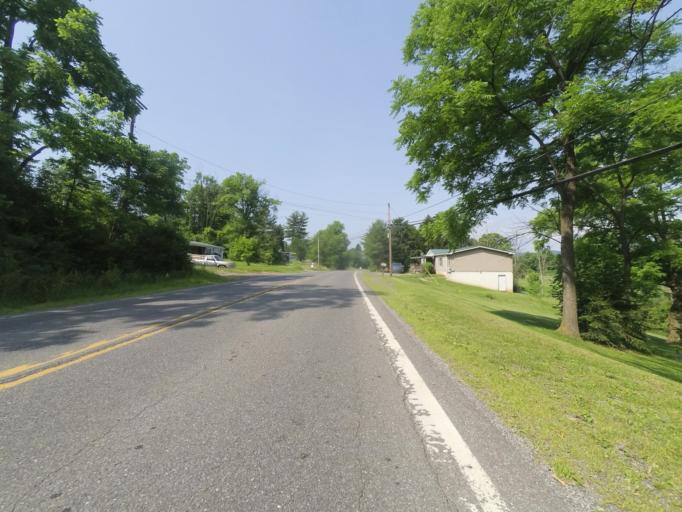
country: US
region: Pennsylvania
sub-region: Centre County
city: Milesburg
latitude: 40.9534
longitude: -77.7523
